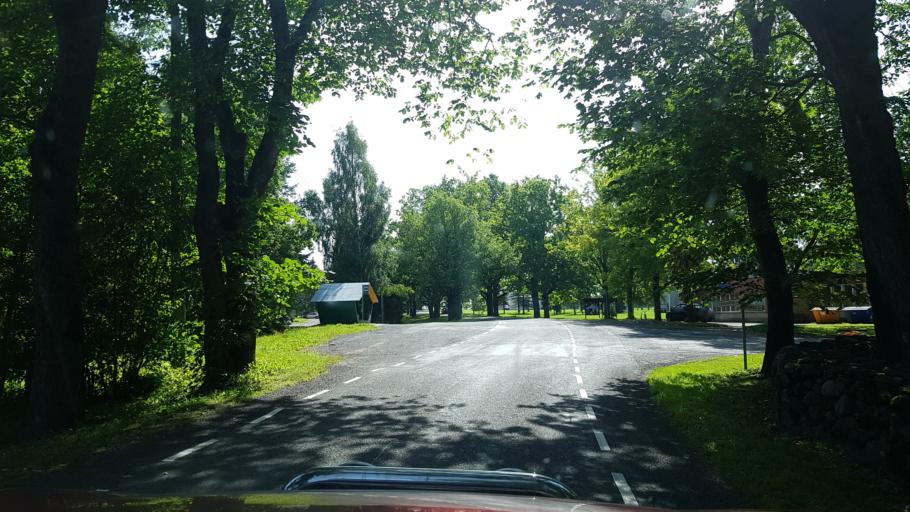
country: EE
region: Viljandimaa
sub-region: Suure-Jaani vald
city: Suure-Jaani
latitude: 58.4858
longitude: 25.5175
